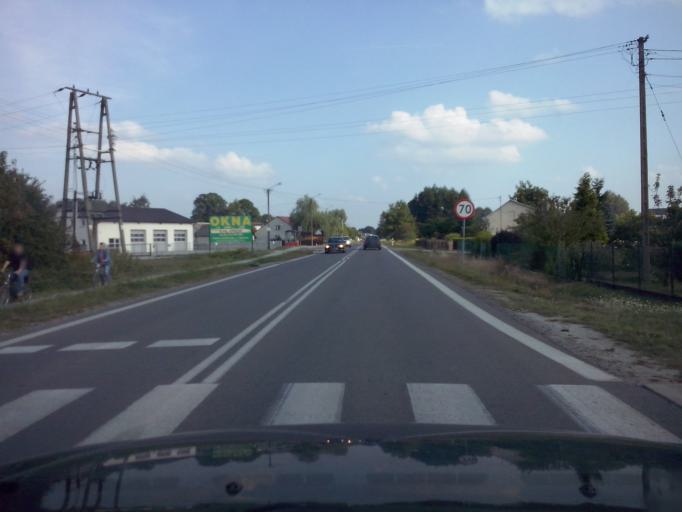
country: PL
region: Subcarpathian Voivodeship
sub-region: Powiat kolbuszowski
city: Kolbuszowa
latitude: 50.2529
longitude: 21.7592
